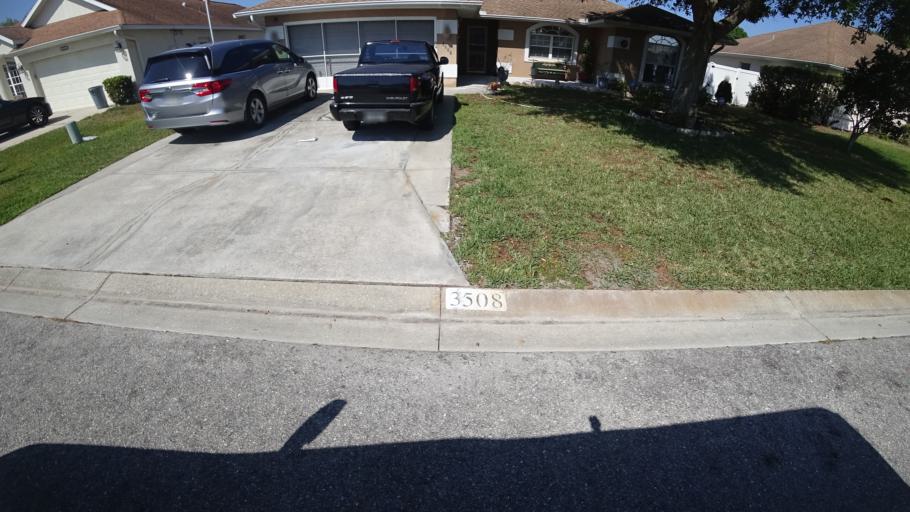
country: US
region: Florida
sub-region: Manatee County
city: Samoset
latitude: 27.4675
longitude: -82.5256
